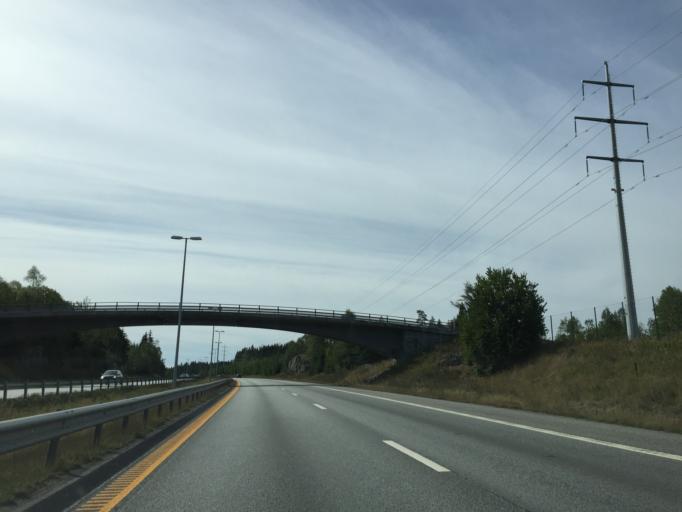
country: NO
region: Akershus
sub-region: Vestby
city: Vestby
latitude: 59.5713
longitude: 10.7235
